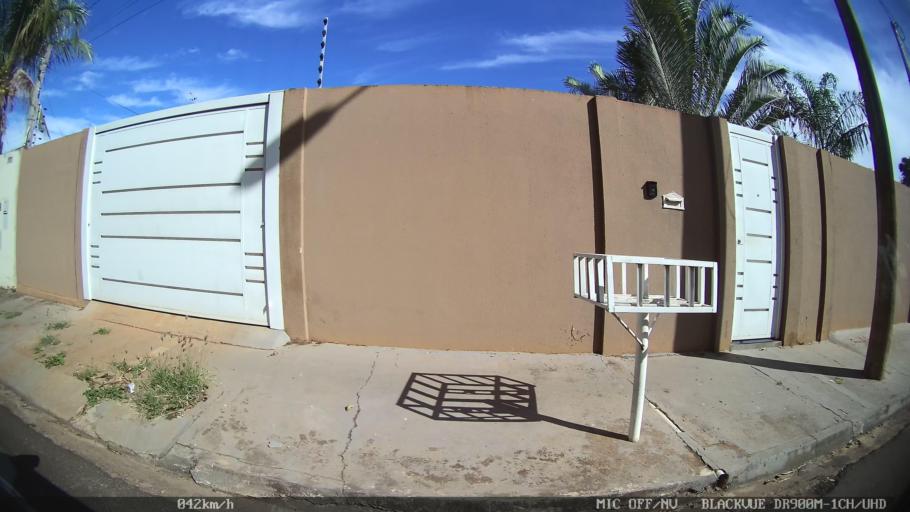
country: BR
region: Sao Paulo
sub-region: Catanduva
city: Catanduva
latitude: -21.1256
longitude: -48.9607
